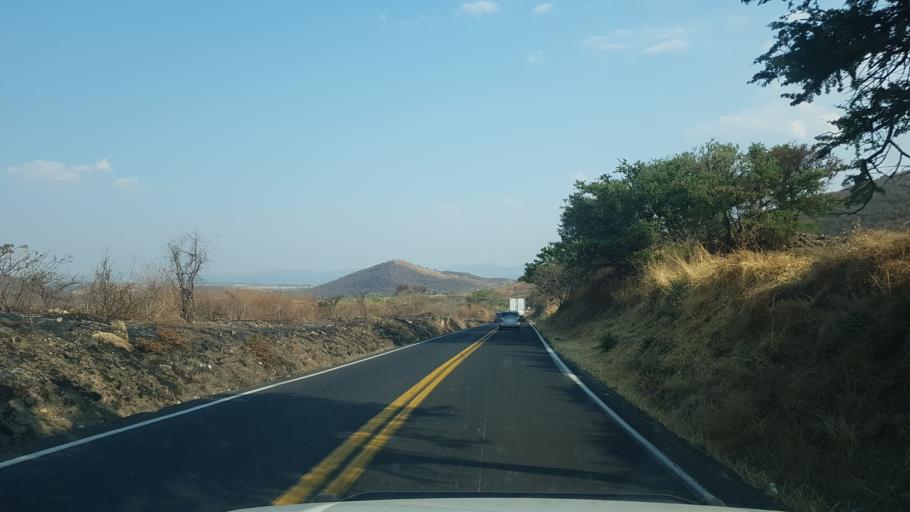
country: MX
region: Puebla
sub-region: Tilapa
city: San Felix Rijo
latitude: 18.6391
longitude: -98.5877
